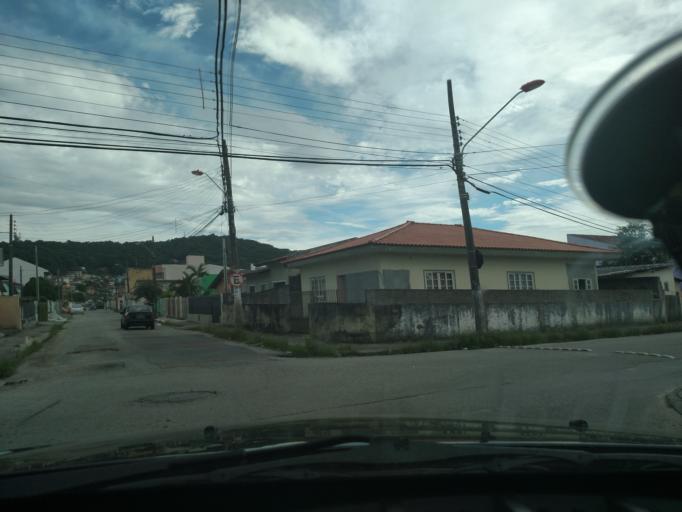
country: BR
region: Santa Catarina
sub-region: Sao Jose
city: Campinas
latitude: -27.6007
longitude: -48.6428
